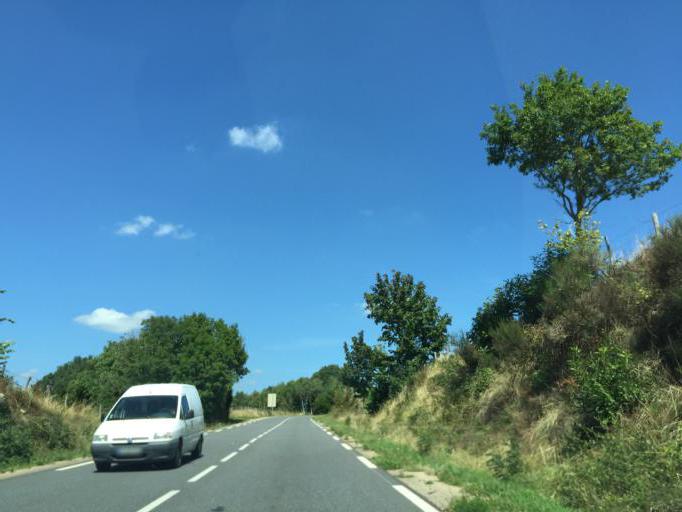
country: FR
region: Midi-Pyrenees
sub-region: Departement de l'Aveyron
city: Espalion
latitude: 44.5673
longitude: 2.7897
